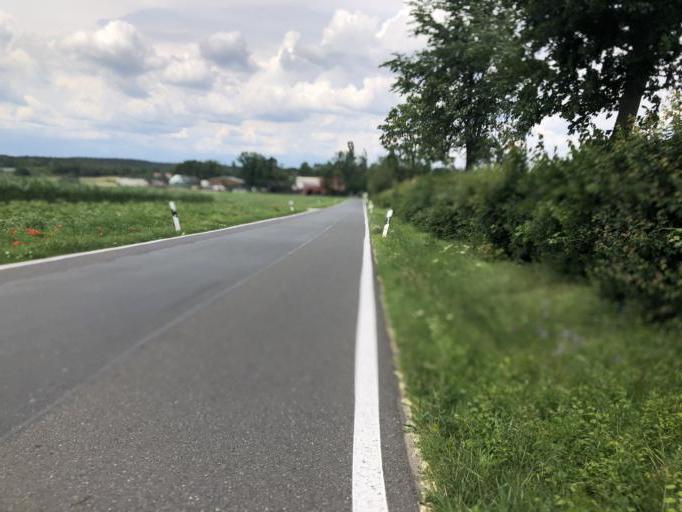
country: DE
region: Bavaria
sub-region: Regierungsbezirk Mittelfranken
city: Hessdorf
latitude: 49.5956
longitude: 10.9344
